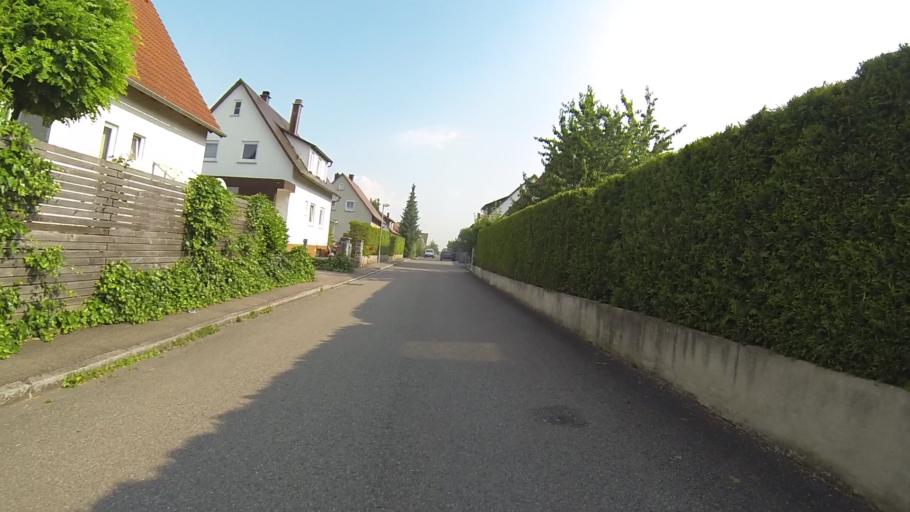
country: DE
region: Baden-Wuerttemberg
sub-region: Tuebingen Region
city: Ulm
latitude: 48.4343
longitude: 9.9720
